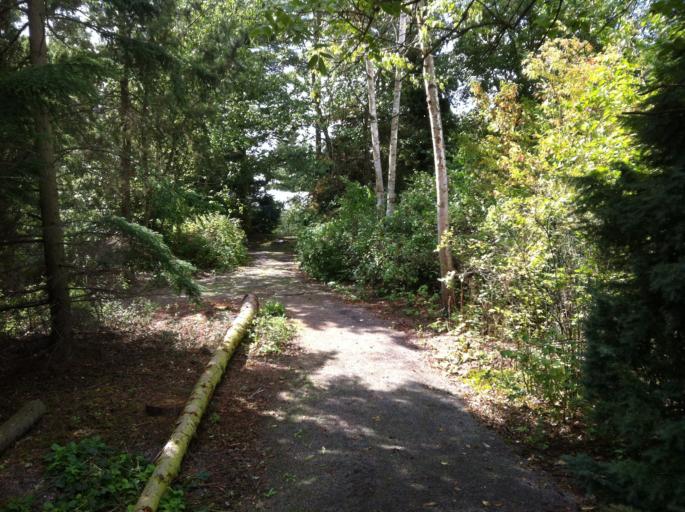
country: DE
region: Bavaria
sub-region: Upper Franconia
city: Bayreuth
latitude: 49.9254
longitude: 11.5866
